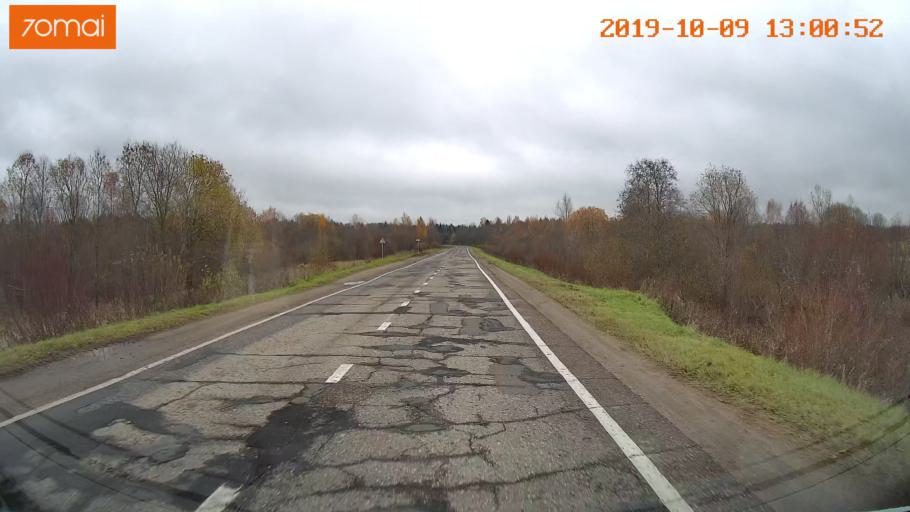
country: RU
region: Jaroslavl
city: Prechistoye
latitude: 58.3734
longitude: 40.4831
